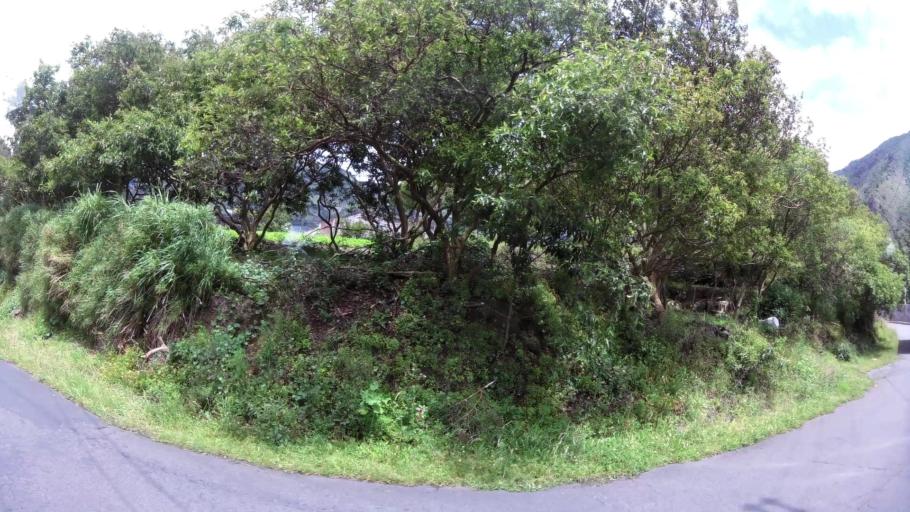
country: EC
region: Tungurahua
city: Banos
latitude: -1.3936
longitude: -78.4113
